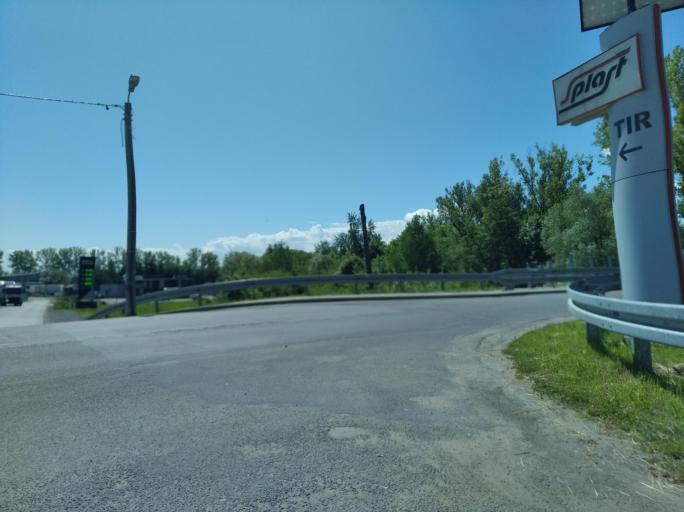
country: PL
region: Subcarpathian Voivodeship
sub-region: Powiat krosnienski
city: Jedlicze
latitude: 49.7099
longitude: 21.6384
